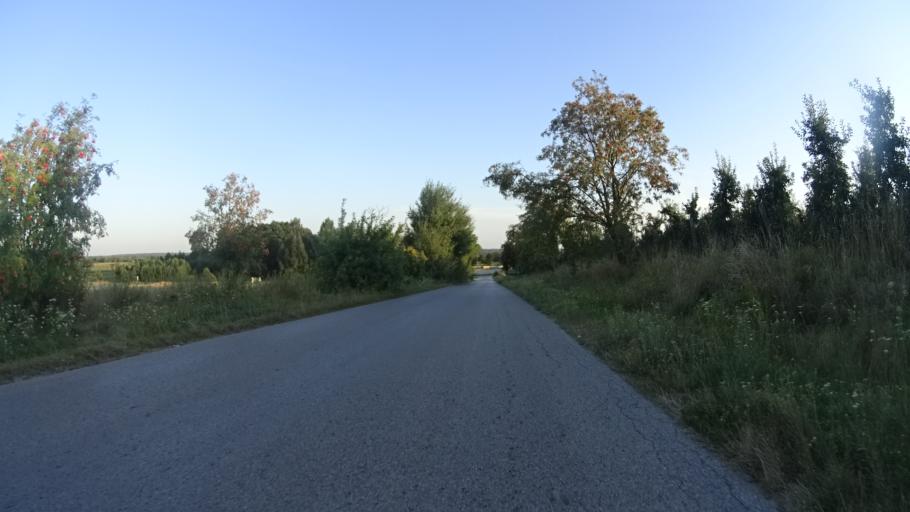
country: PL
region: Masovian Voivodeship
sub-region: Powiat bialobrzeski
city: Wysmierzyce
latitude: 51.6630
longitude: 20.8311
